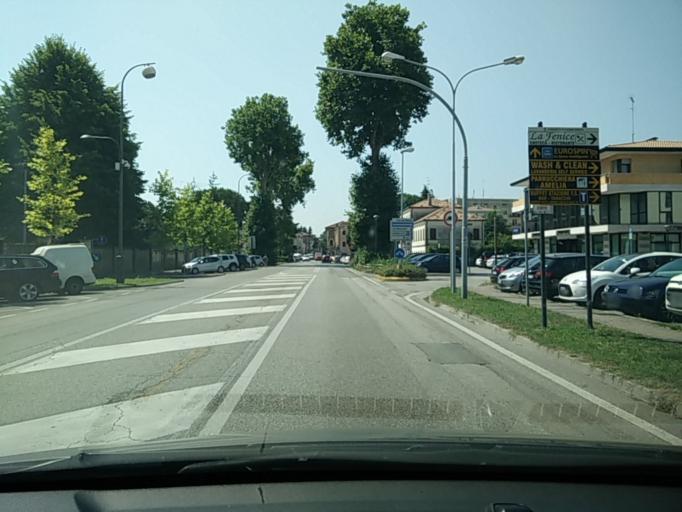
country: IT
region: Veneto
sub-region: Provincia di Treviso
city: Mogliano Veneto
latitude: 45.5635
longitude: 12.2351
